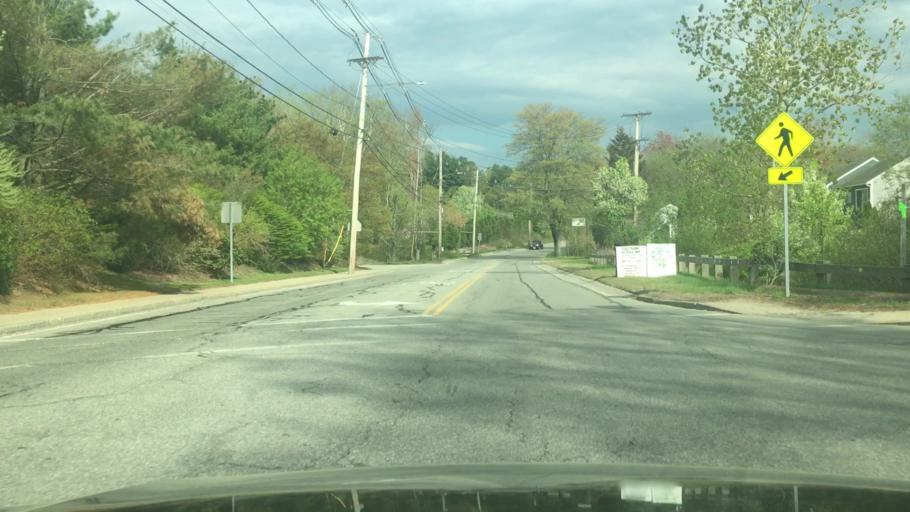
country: US
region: Massachusetts
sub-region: Middlesex County
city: North Reading
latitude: 42.5769
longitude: -71.1084
